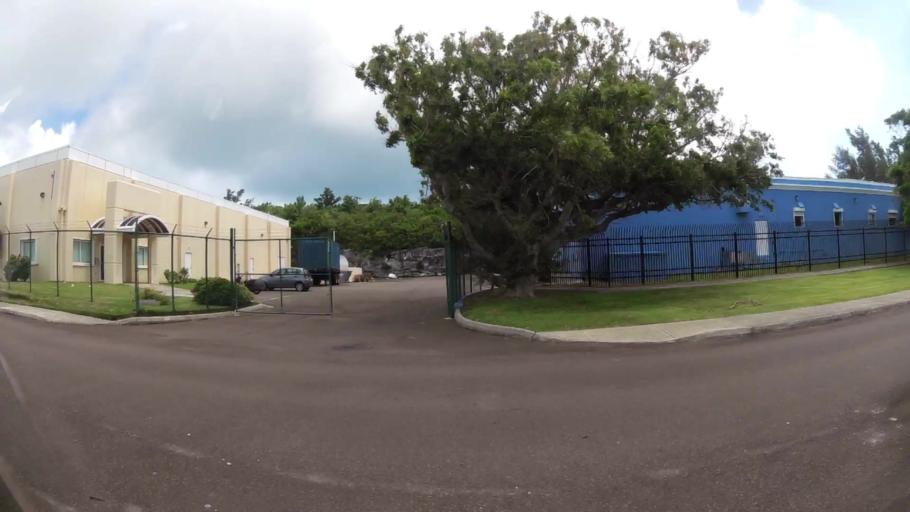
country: BM
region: Saint George
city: Saint George
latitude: 32.3660
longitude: -64.6691
